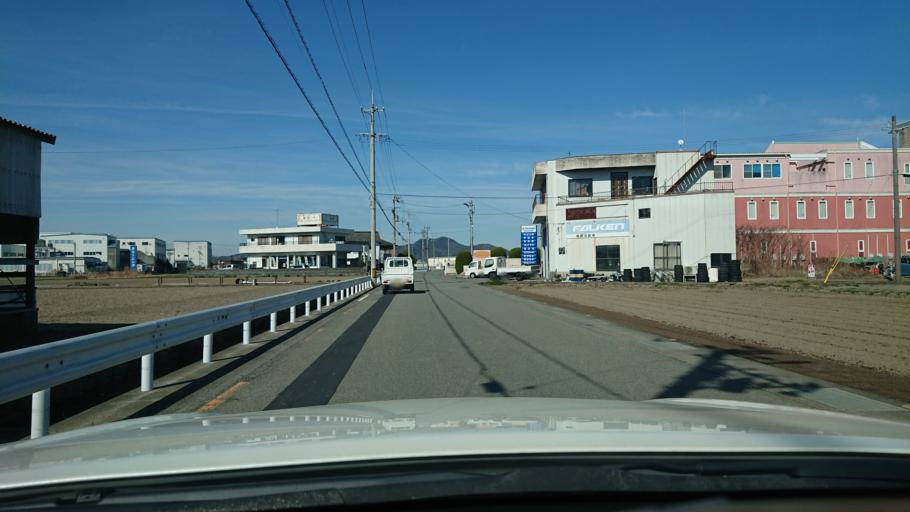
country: JP
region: Tokushima
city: Komatsushimacho
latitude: 33.9857
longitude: 134.5887
